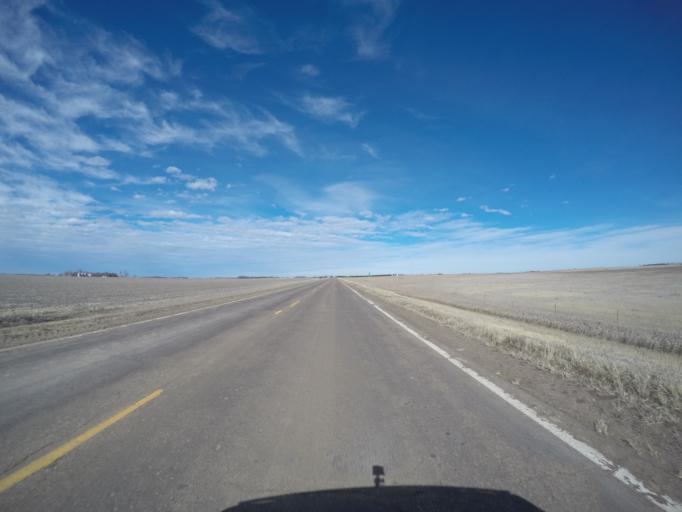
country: US
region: Nebraska
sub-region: Franklin County
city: Franklin
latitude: 40.1854
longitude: -98.9525
